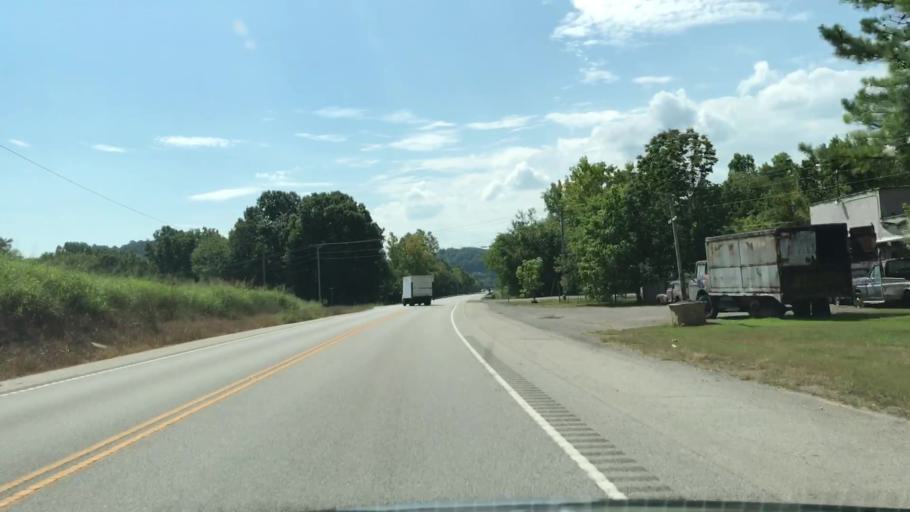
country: US
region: Tennessee
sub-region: Smith County
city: Carthage
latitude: 36.3160
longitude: -86.0103
